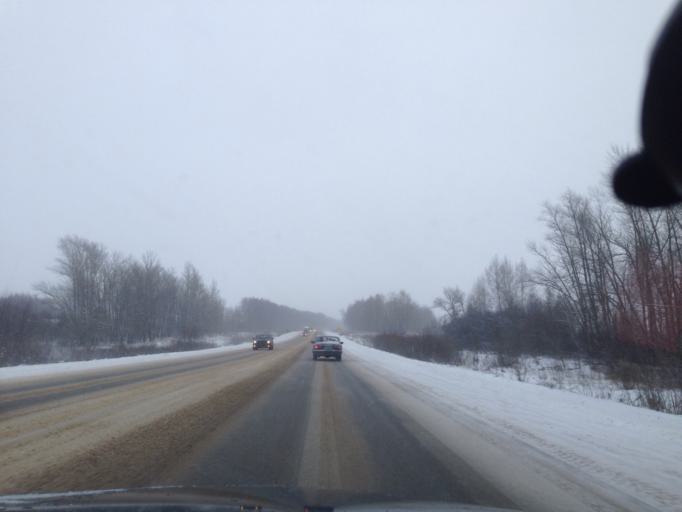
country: RU
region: Tula
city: Bolokhovo
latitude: 54.0766
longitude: 37.7864
